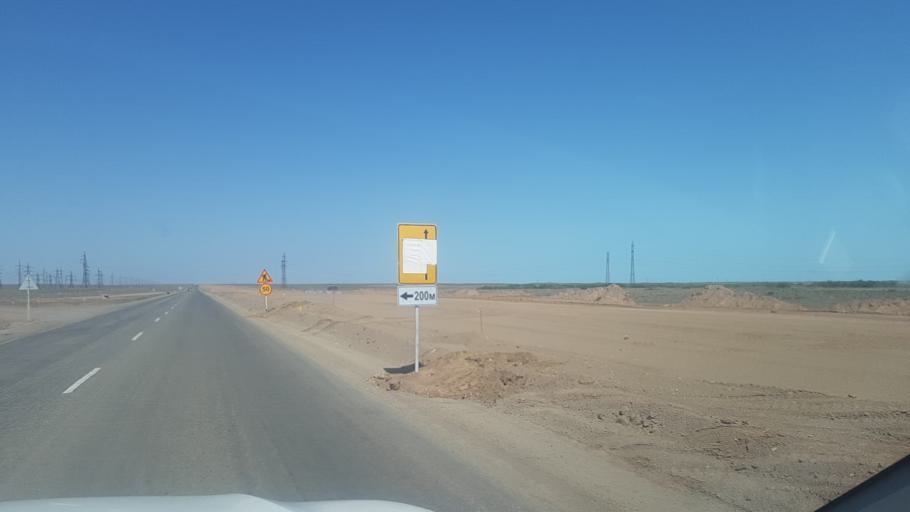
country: KZ
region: Qaraghandy
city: Balqash
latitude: 46.7190
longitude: 74.4761
